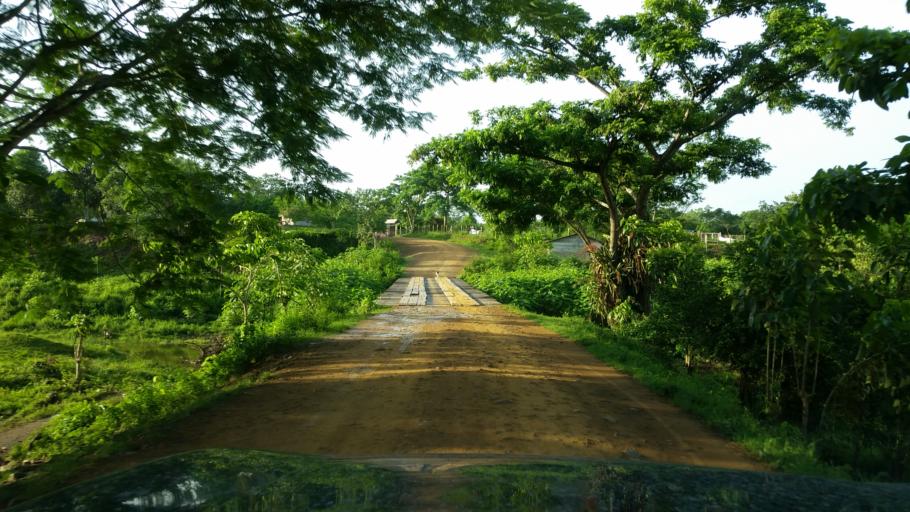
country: NI
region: Atlantico Norte (RAAN)
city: Puerto Cabezas
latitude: 14.0687
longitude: -83.9868
